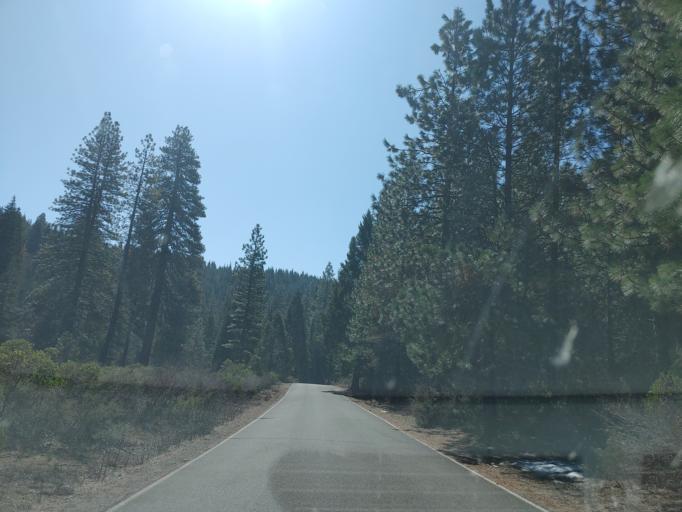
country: US
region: California
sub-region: Siskiyou County
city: McCloud
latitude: 41.2434
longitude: -122.0271
